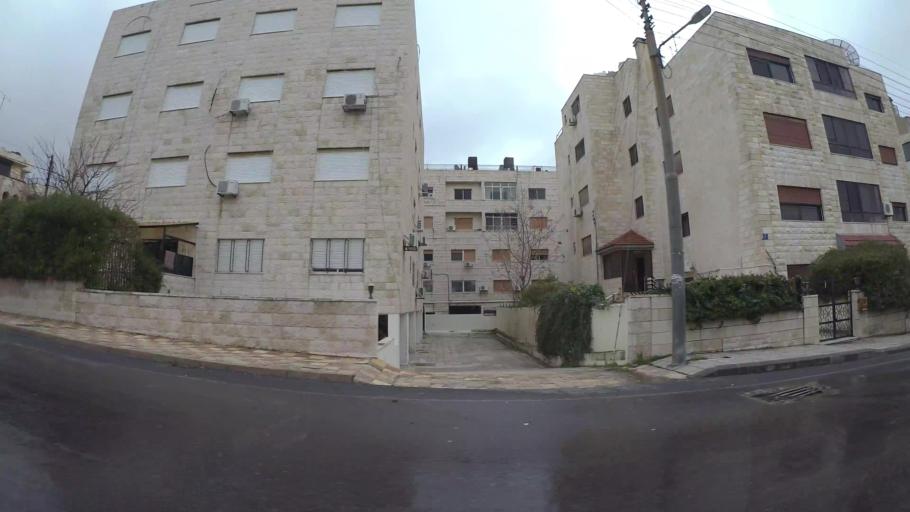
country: JO
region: Amman
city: Wadi as Sir
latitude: 31.9525
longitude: 35.8682
